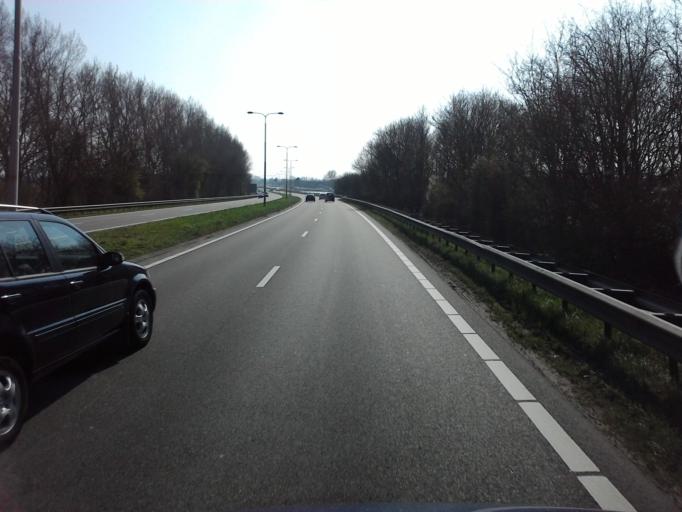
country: NL
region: North Holland
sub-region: Gemeente Zaanstad
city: Zaanstad
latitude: 52.4915
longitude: 4.7734
